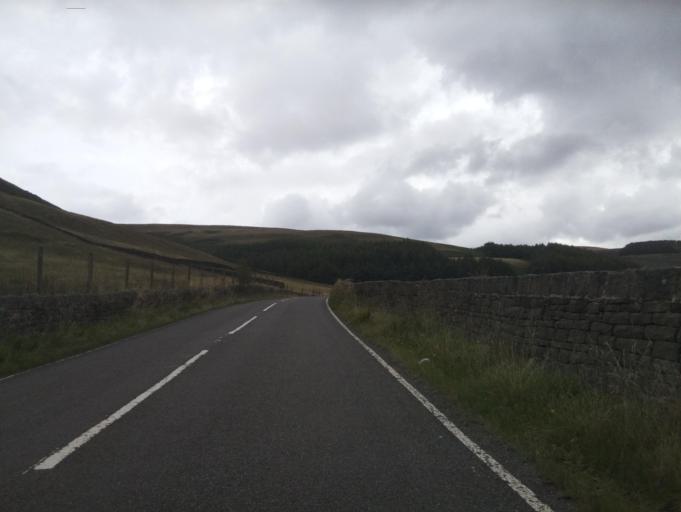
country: GB
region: England
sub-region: Kirklees
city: Meltham
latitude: 53.4979
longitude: -1.8626
